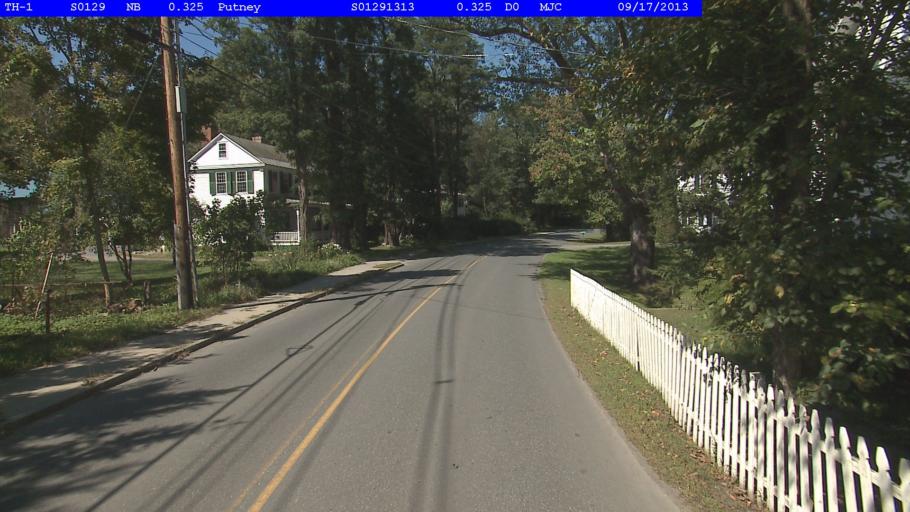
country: US
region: New Hampshire
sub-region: Cheshire County
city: Westmoreland
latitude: 42.9777
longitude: -72.5269
